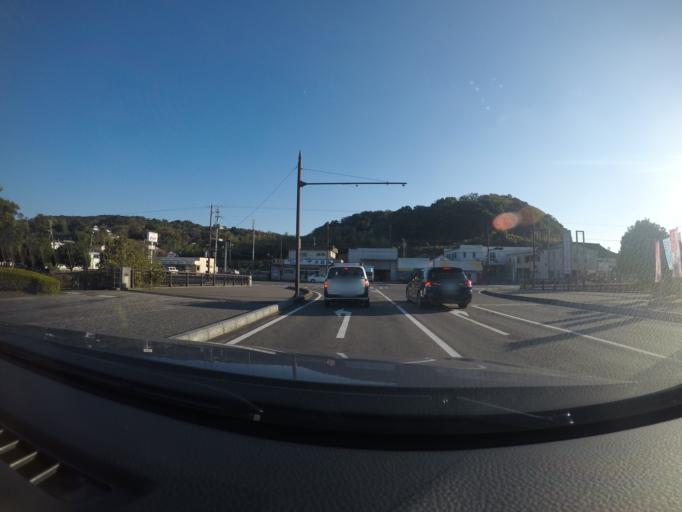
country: JP
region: Kumamoto
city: Minamata
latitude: 32.1991
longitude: 130.3841
